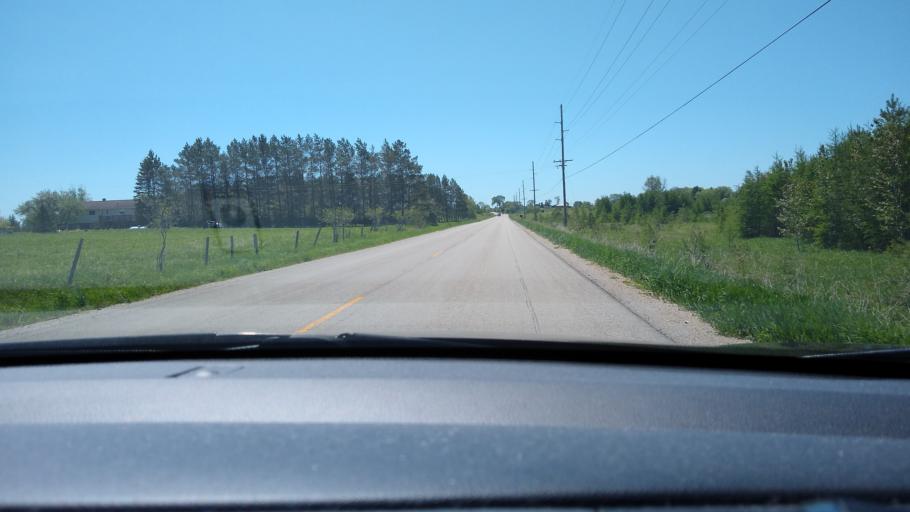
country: US
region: Michigan
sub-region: Delta County
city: Escanaba
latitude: 45.8469
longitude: -87.1841
